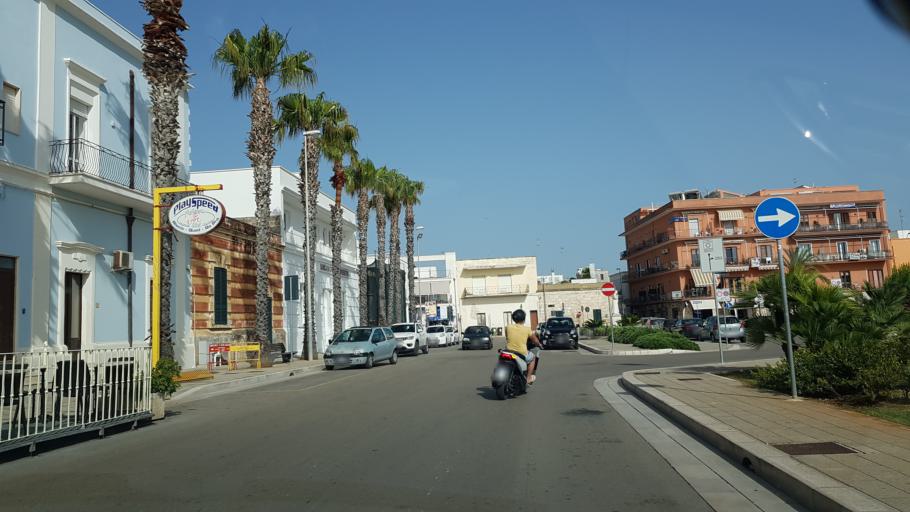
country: IT
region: Apulia
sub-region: Provincia di Lecce
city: Porto Cesareo
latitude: 40.2602
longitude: 17.8912
